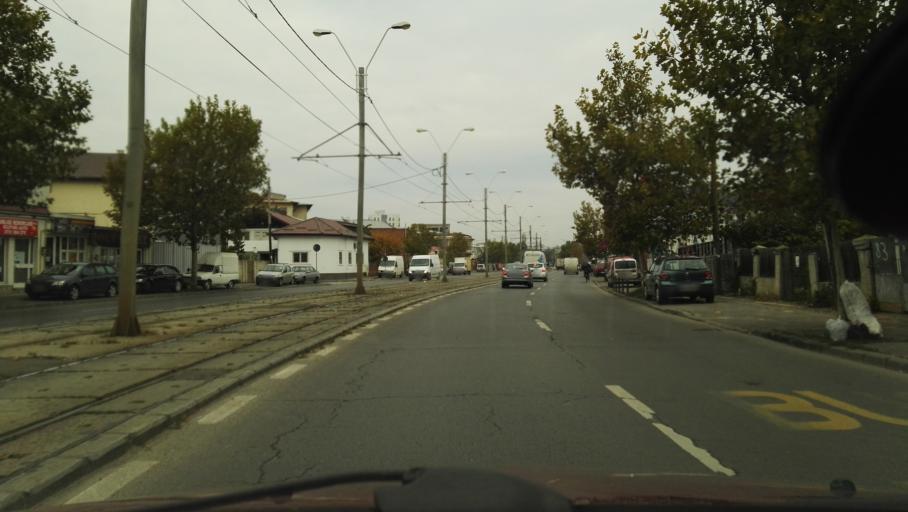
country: RO
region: Bucuresti
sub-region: Municipiul Bucuresti
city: Bucuresti
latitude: 44.4086
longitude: 26.0907
